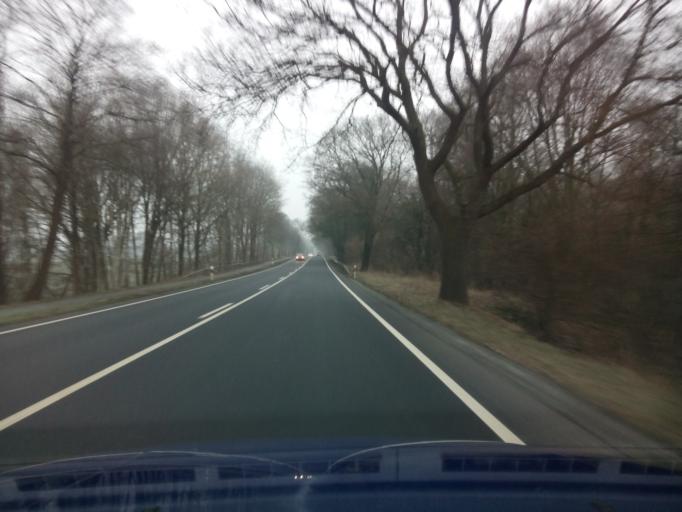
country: DE
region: Lower Saxony
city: Ritterhude
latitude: 53.2342
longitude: 8.7100
